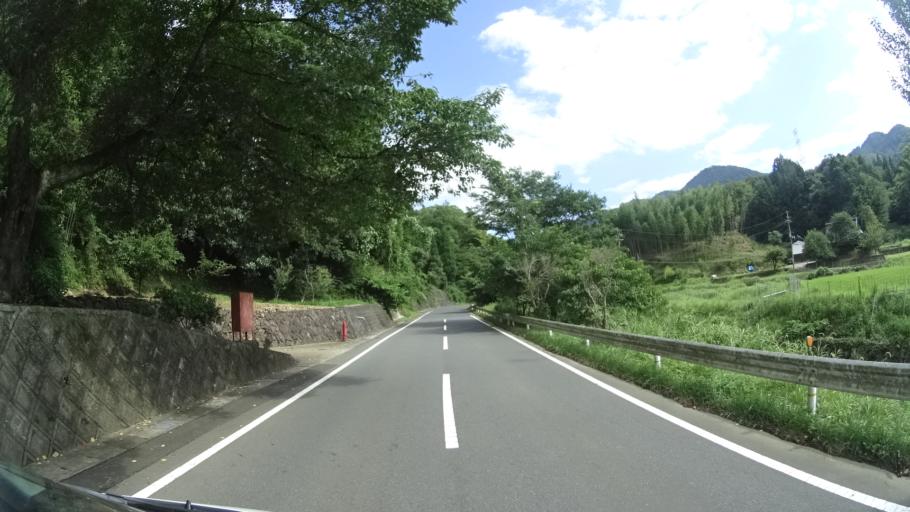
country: JP
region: Kyoto
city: Fukuchiyama
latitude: 35.3636
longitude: 135.1341
